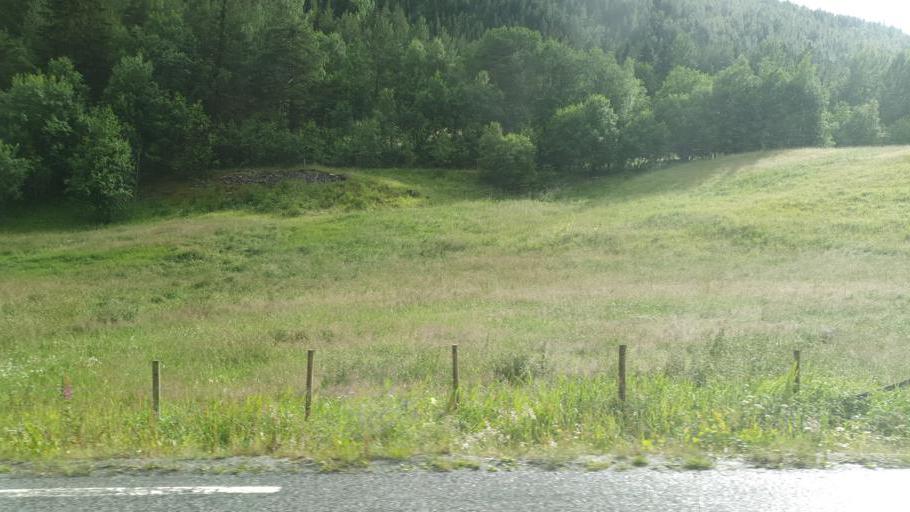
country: NO
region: Oppland
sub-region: Dovre
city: Dovre
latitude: 61.8531
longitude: 9.2832
